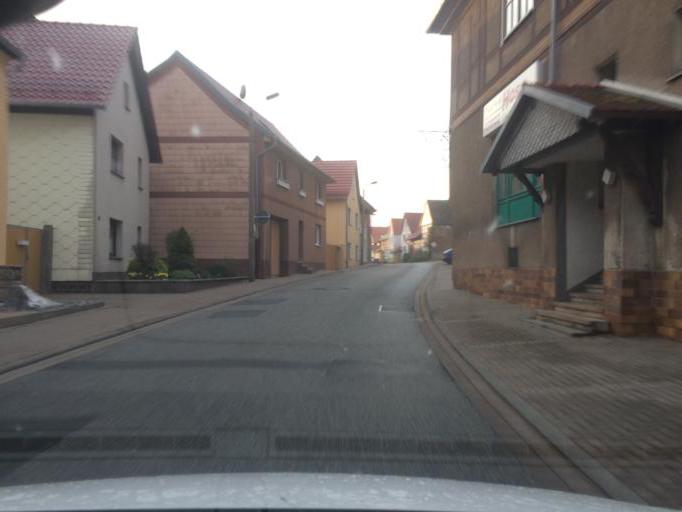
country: DE
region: Thuringia
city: Weissenborn-Luderode
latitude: 51.5329
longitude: 10.4163
